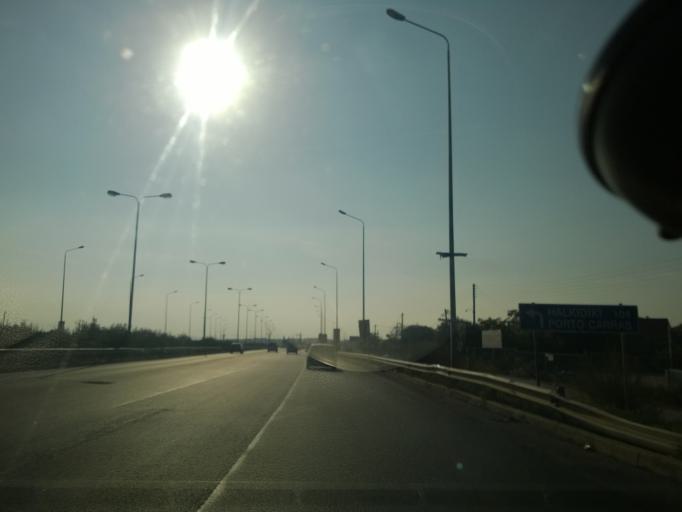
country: GR
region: Central Macedonia
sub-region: Nomos Thessalonikis
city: Pylaia
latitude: 40.5846
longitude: 22.9809
